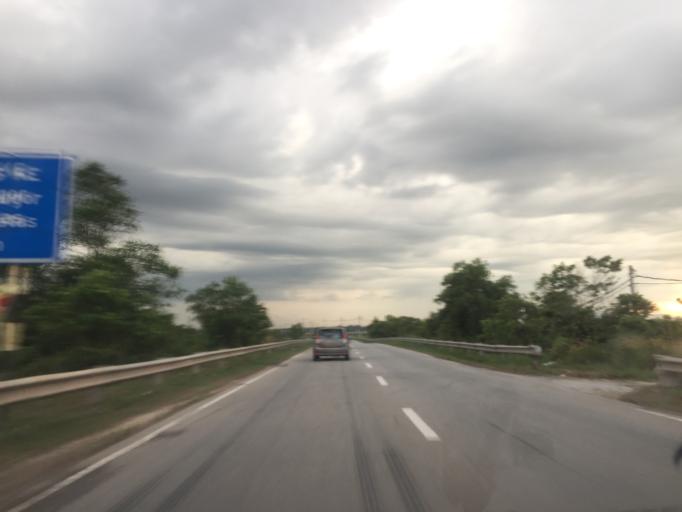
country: MY
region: Penang
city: Tasek Glugor
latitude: 5.5629
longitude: 100.5027
